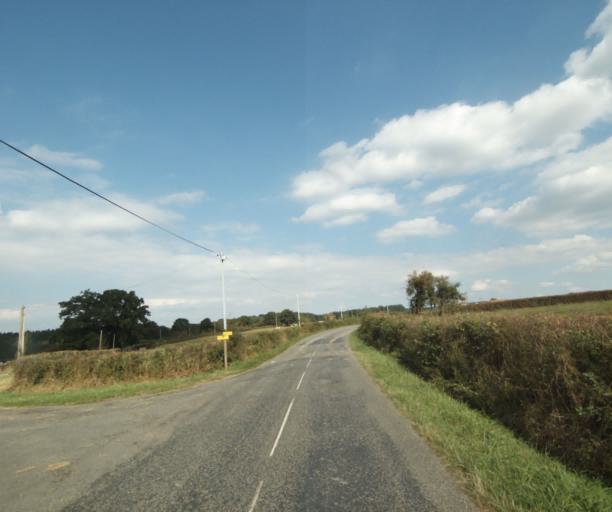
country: FR
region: Bourgogne
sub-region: Departement de Saone-et-Loire
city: Palinges
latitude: 46.4999
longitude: 4.2267
